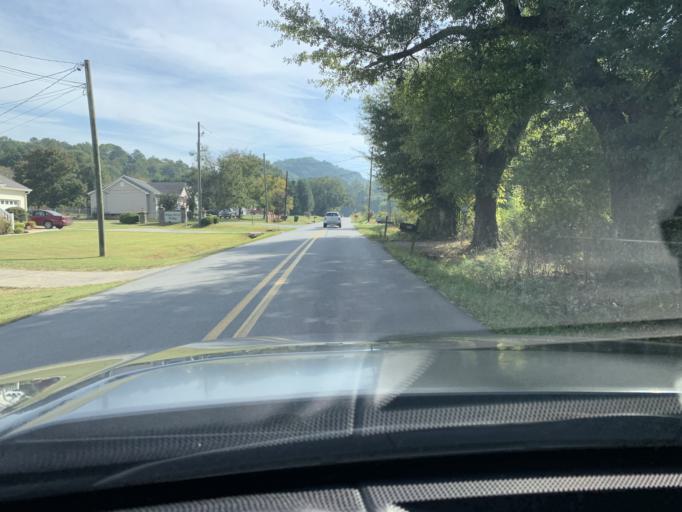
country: US
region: Georgia
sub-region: Polk County
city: Aragon
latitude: 34.0357
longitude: -85.0375
